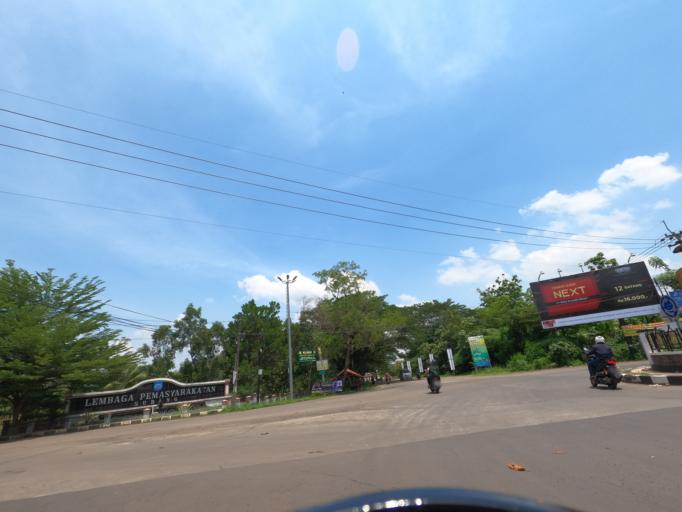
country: ID
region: West Java
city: Pamanukan
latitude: -6.5506
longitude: 107.7647
